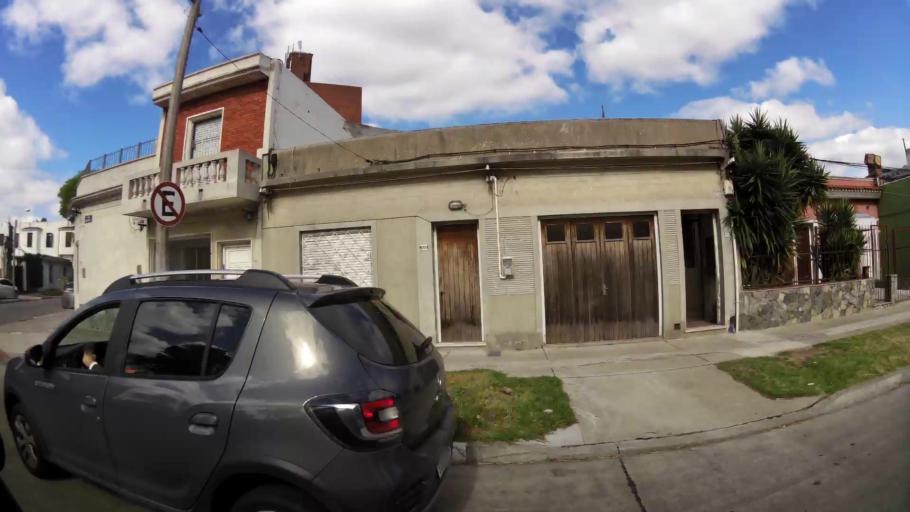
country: UY
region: Montevideo
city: Montevideo
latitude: -34.8823
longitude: -56.1649
